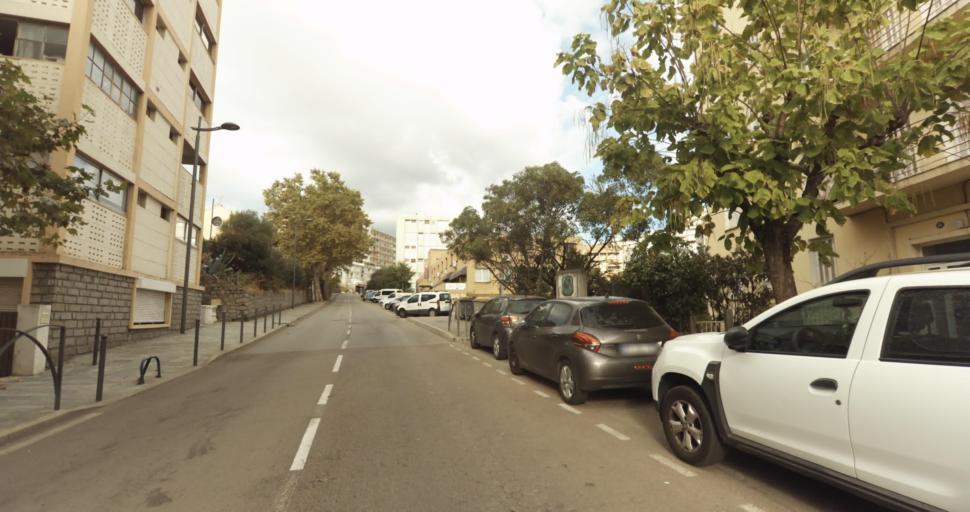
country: FR
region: Corsica
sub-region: Departement de la Corse-du-Sud
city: Ajaccio
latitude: 41.9285
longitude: 8.7366
